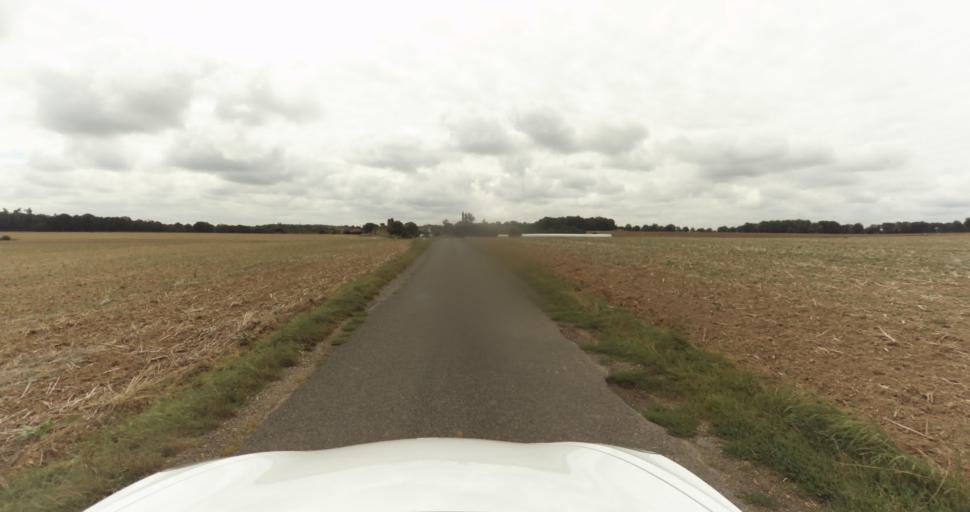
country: FR
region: Haute-Normandie
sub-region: Departement de l'Eure
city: Saint-Sebastien-de-Morsent
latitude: 49.0223
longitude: 1.0606
